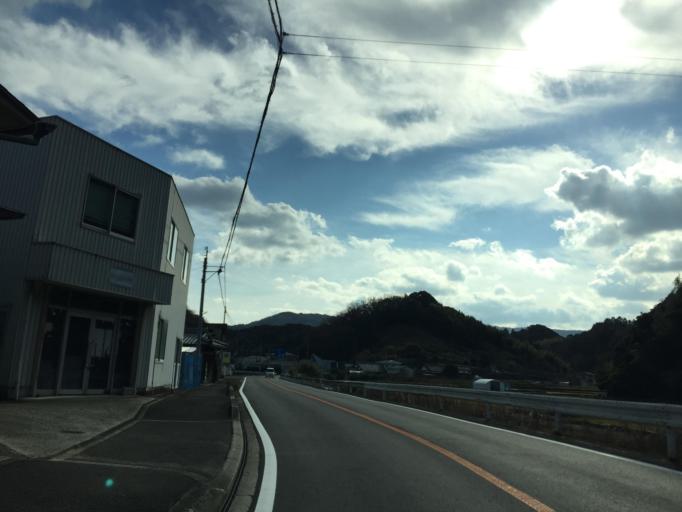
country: JP
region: Wakayama
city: Kainan
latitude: 34.1679
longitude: 135.2504
